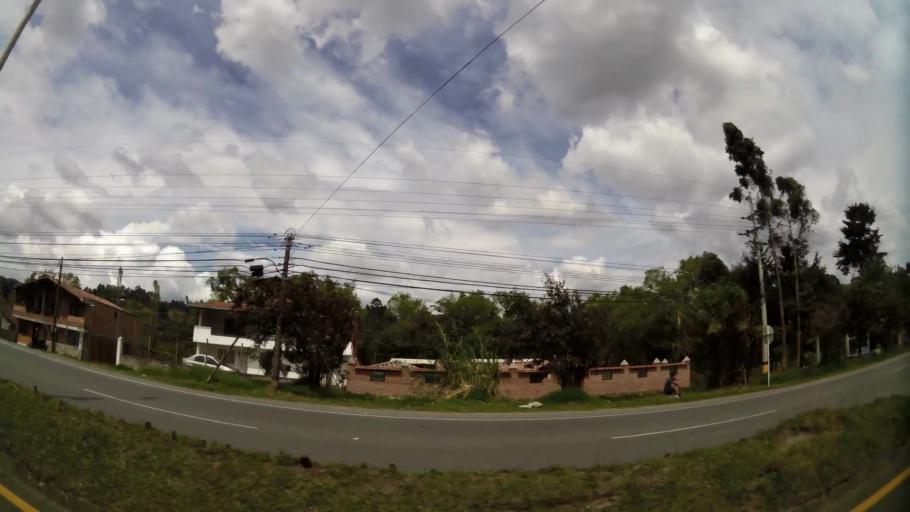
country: CO
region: Antioquia
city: Guarne
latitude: 6.2933
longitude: -75.4524
